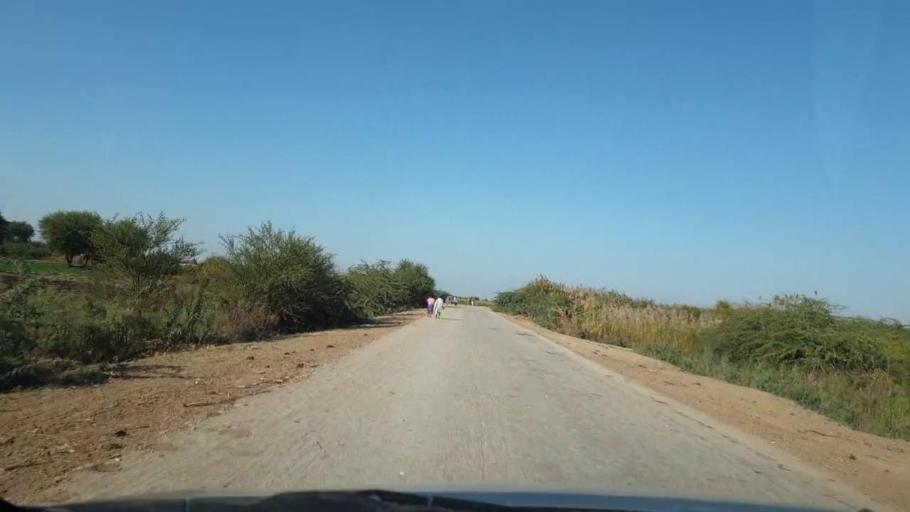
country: PK
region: Sindh
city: Berani
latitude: 25.8182
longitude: 68.9480
